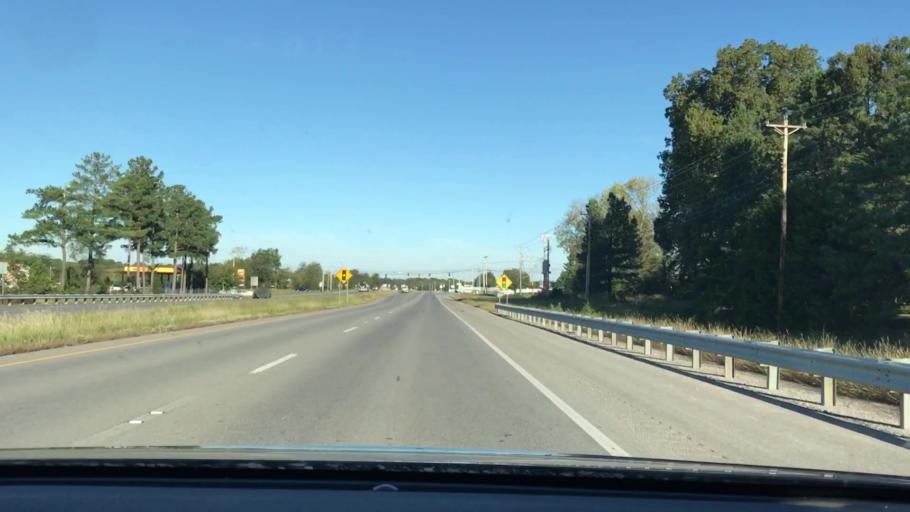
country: US
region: Kentucky
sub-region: Christian County
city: Hopkinsville
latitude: 36.8200
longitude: -87.5021
